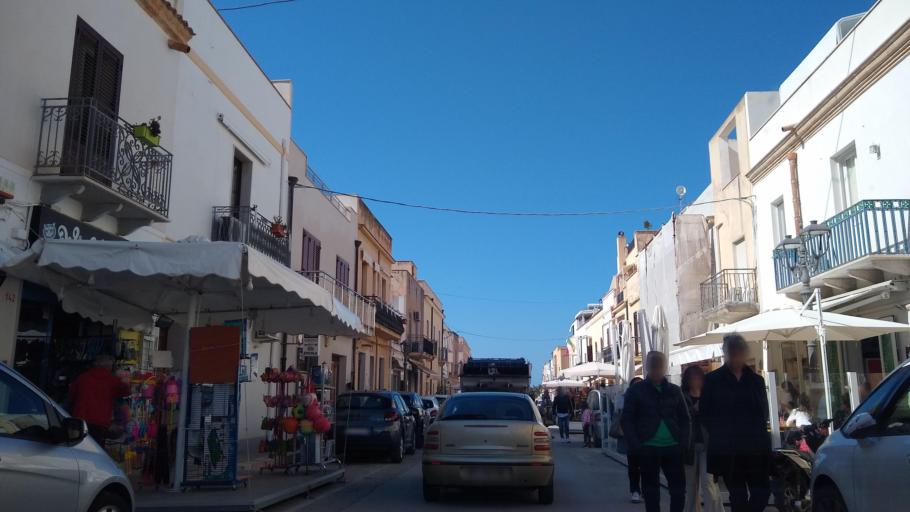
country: IT
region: Sicily
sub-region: Trapani
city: San Vito Lo Capo
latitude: 38.1742
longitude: 12.7339
